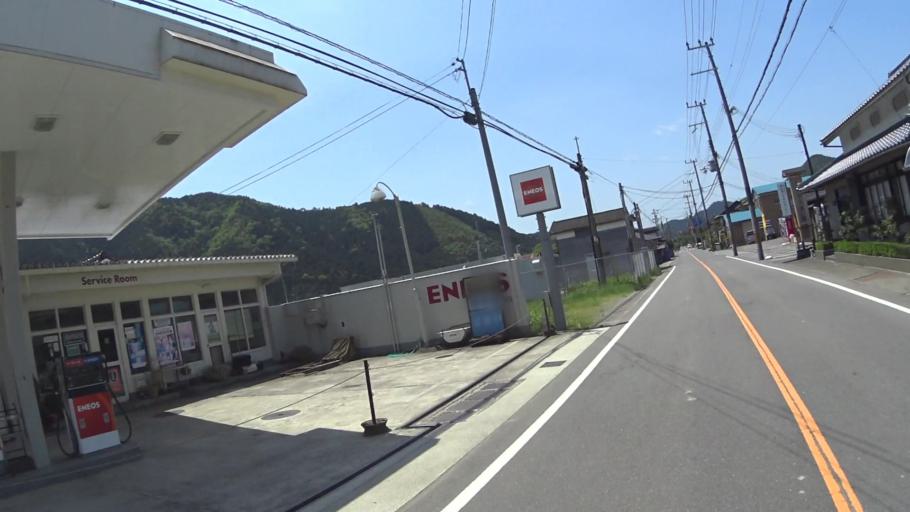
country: JP
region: Kyoto
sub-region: Kyoto-shi
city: Kamigyo-ku
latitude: 35.1793
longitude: 135.6594
